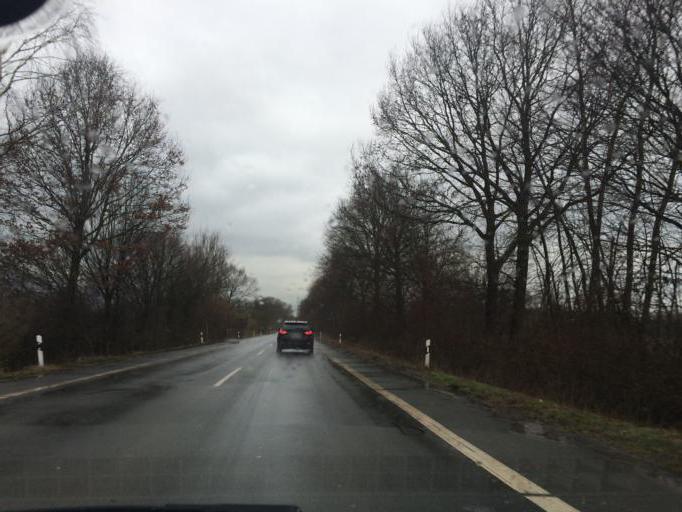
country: DE
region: North Rhine-Westphalia
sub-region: Regierungsbezirk Munster
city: Gladbeck
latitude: 51.6120
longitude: 6.9571
